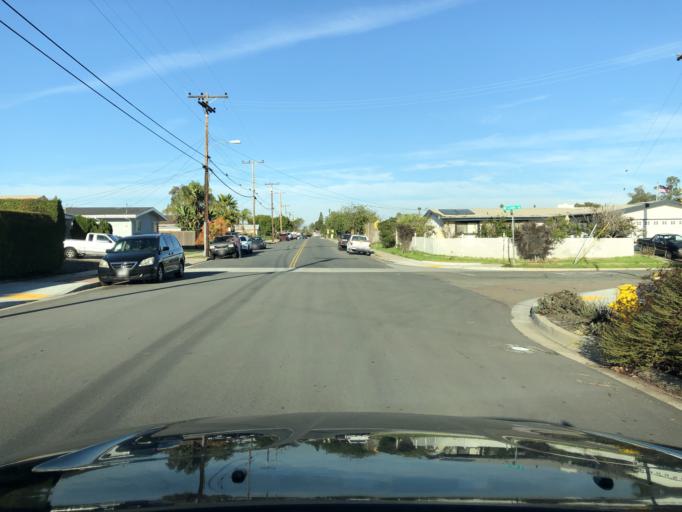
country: US
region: California
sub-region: San Diego County
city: La Jolla
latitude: 32.8216
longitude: -117.1953
